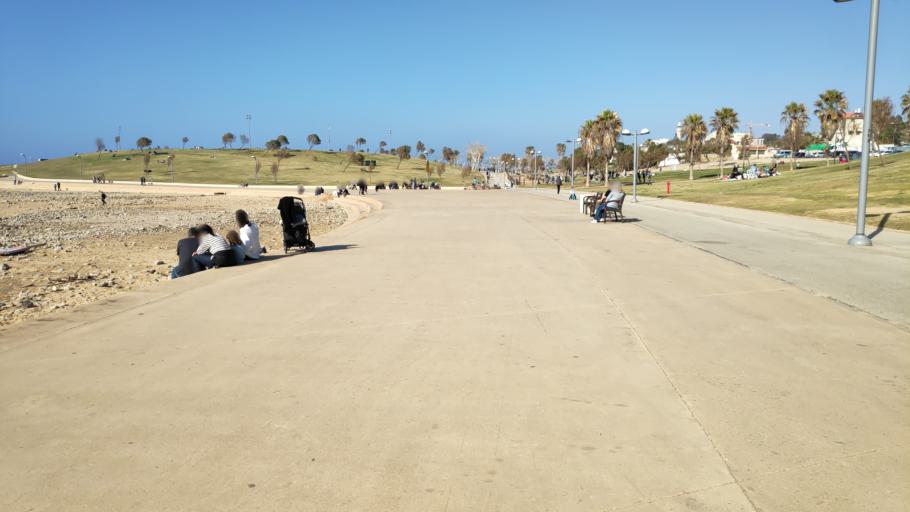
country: IL
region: Tel Aviv
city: Yafo
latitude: 32.0435
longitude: 34.7464
